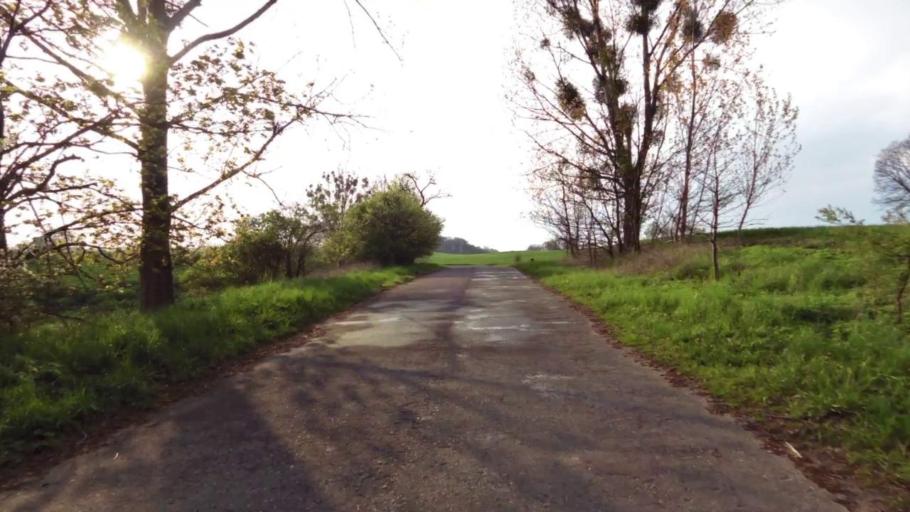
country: PL
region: West Pomeranian Voivodeship
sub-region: Powiat mysliborski
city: Mysliborz
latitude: 52.8998
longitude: 14.7675
